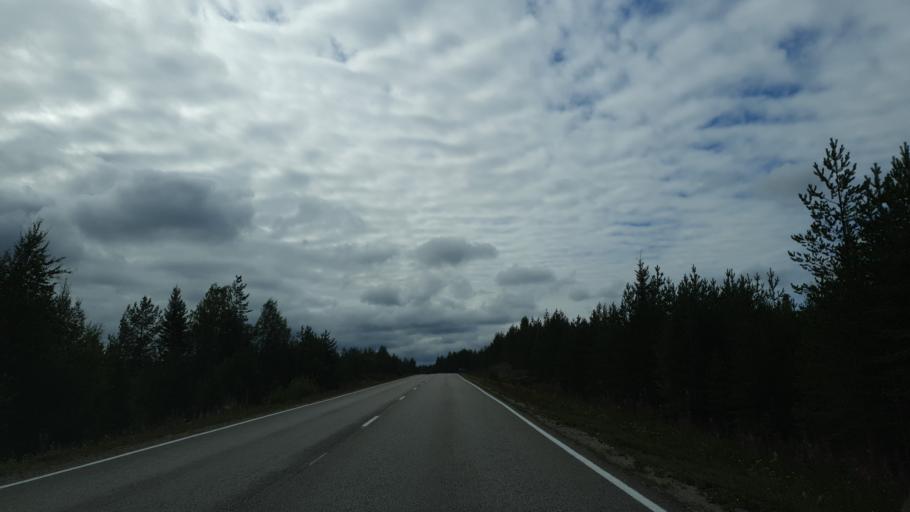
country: FI
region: Kainuu
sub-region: Kehys-Kainuu
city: Kuhmo
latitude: 64.1934
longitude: 29.1806
